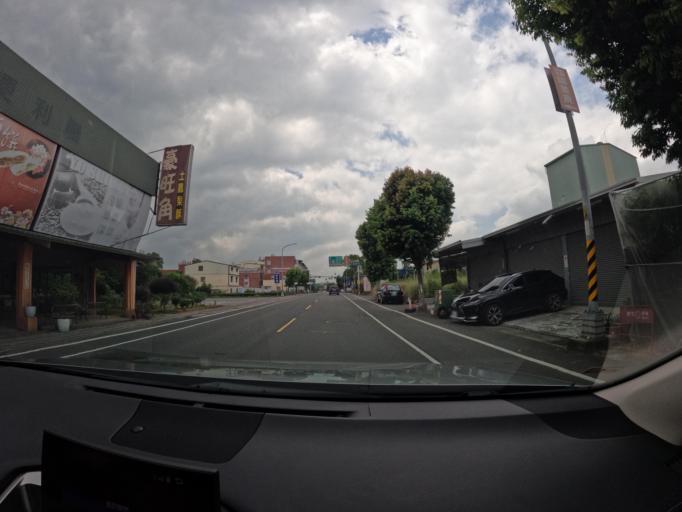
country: TW
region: Taiwan
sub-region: Nantou
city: Nantou
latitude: 23.9098
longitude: 120.6371
